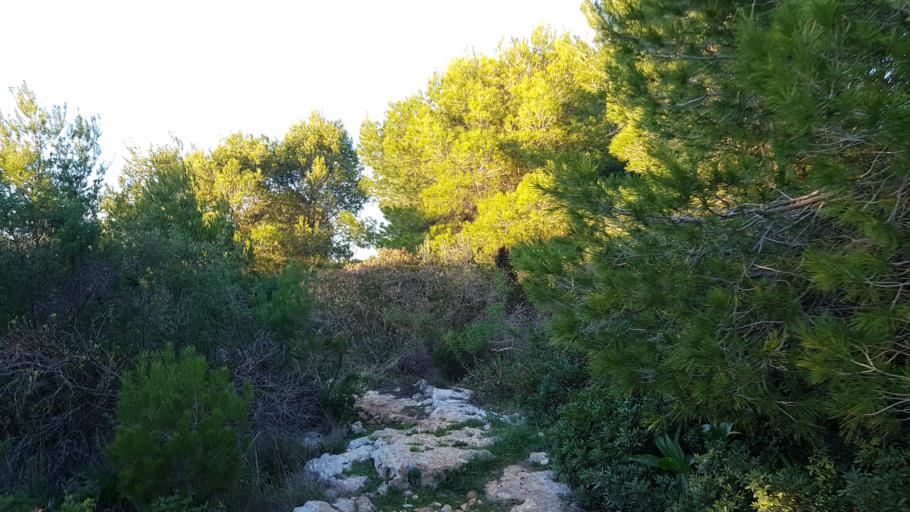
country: IT
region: Apulia
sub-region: Provincia di Lecce
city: Nardo
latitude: 40.1543
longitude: 17.9613
